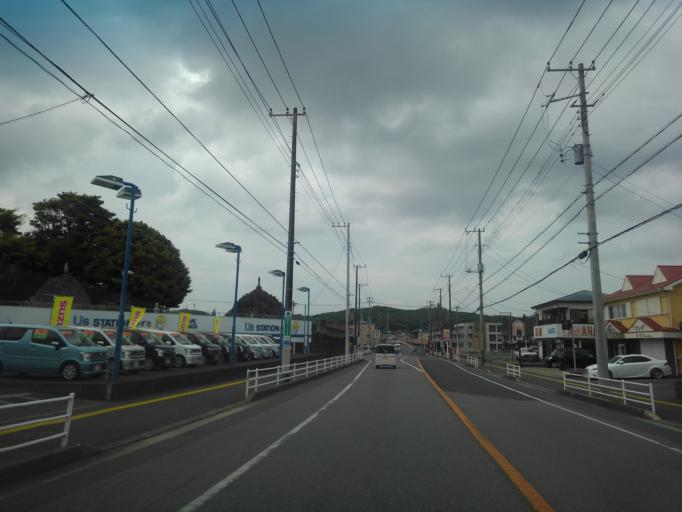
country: JP
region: Chiba
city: Kimitsu
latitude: 35.3310
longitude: 139.9179
